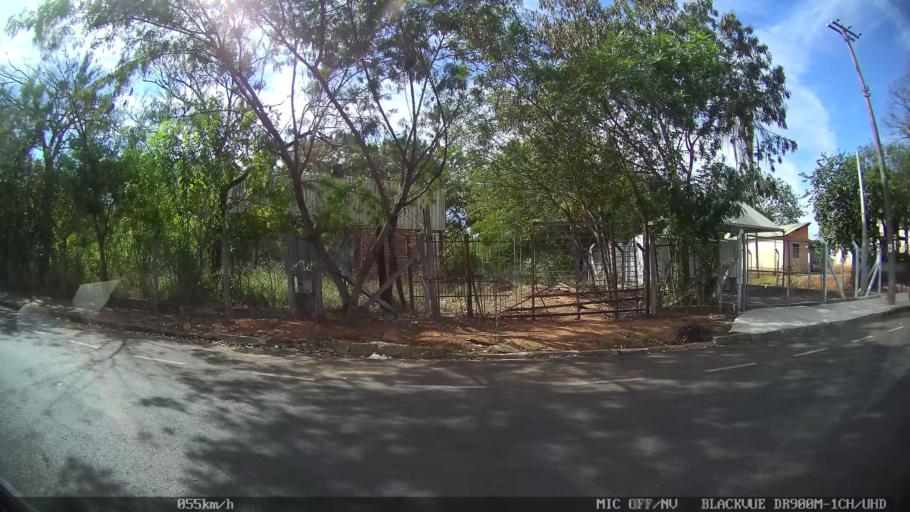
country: BR
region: Sao Paulo
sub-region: Sao Jose Do Rio Preto
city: Sao Jose do Rio Preto
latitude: -20.8395
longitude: -49.3438
